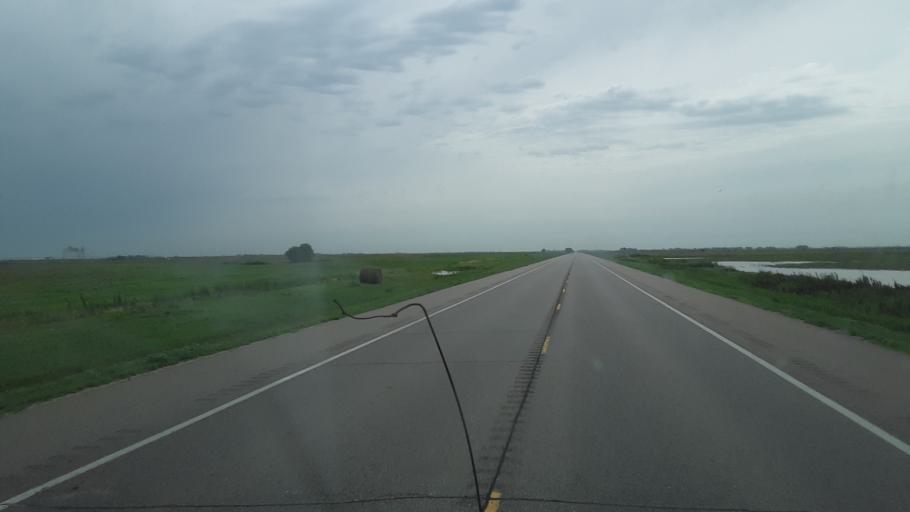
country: US
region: Kansas
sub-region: Stafford County
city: Saint John
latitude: 37.9563
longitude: -98.9080
